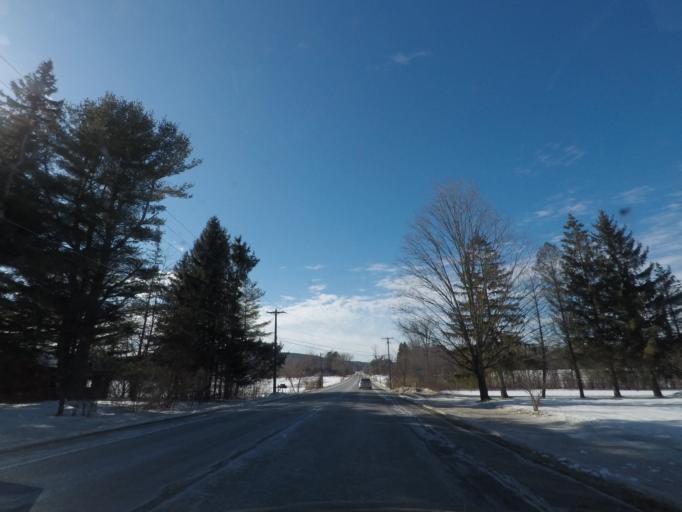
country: US
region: New York
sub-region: Albany County
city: Altamont
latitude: 42.7379
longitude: -74.0029
